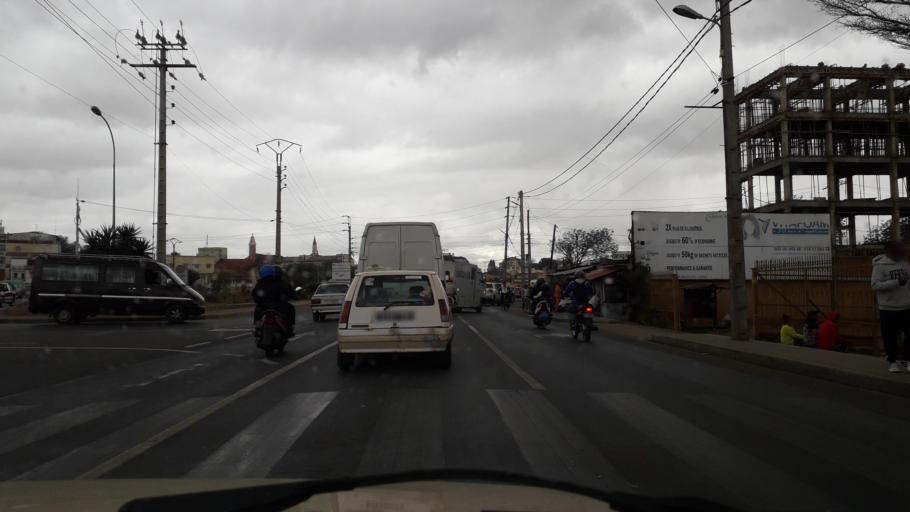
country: MG
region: Analamanga
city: Antananarivo
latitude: -18.8927
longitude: 47.5220
